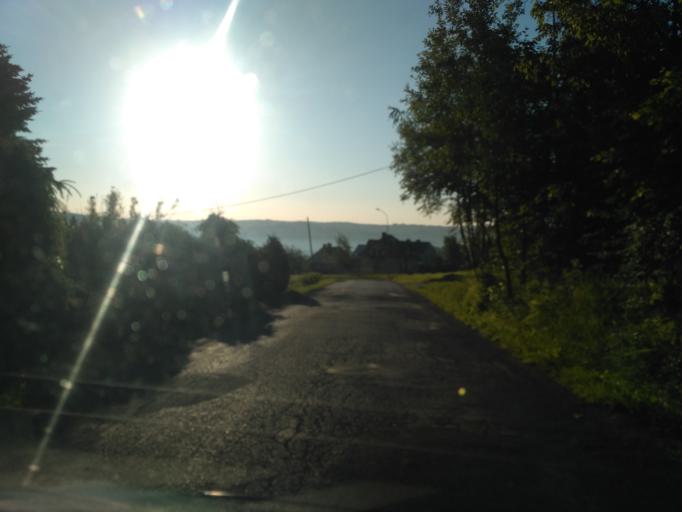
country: PL
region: Subcarpathian Voivodeship
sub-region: Powiat strzyzowski
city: Polomia
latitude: 49.8913
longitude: 21.8575
